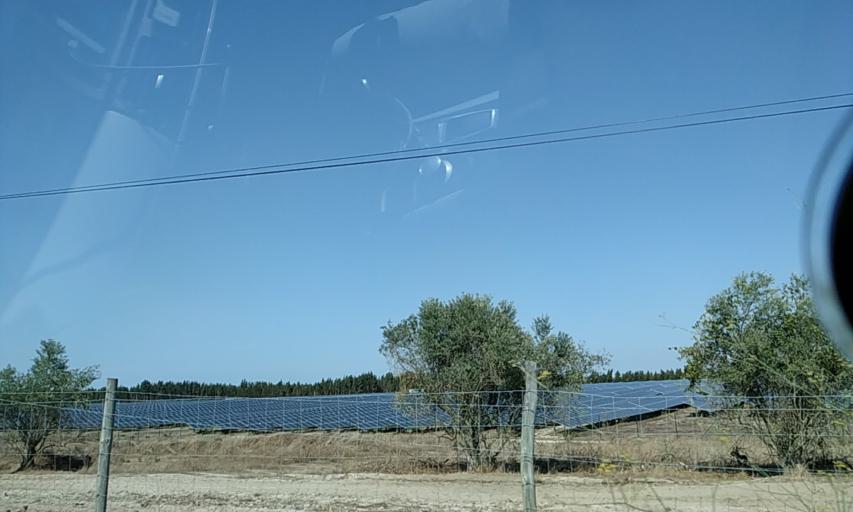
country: PT
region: Evora
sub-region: Vendas Novas
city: Vendas Novas
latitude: 38.7271
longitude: -8.6218
